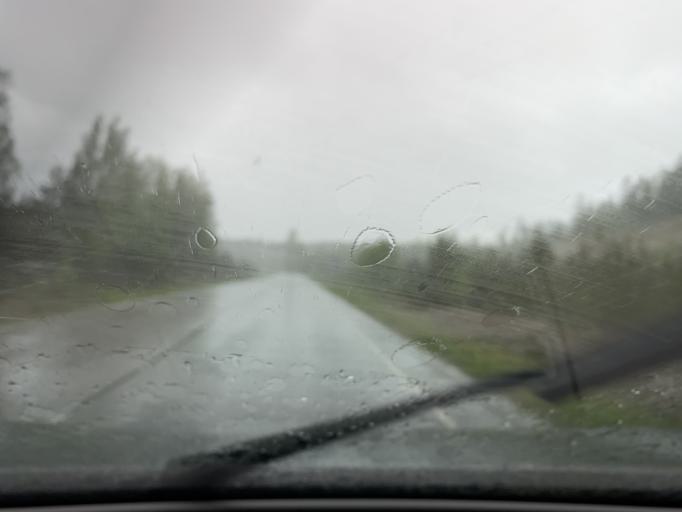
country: FI
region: Paijanne Tavastia
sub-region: Lahti
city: Jaervelae
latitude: 60.8017
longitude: 25.3817
